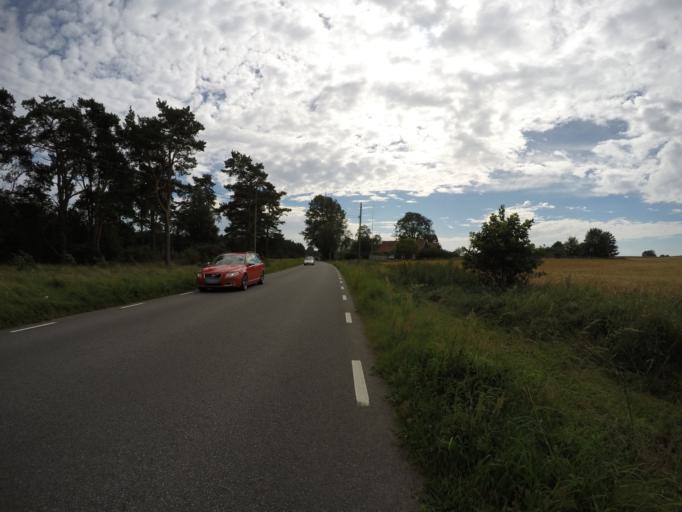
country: SE
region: Skane
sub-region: Simrishamns Kommun
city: Simrishamn
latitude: 55.4329
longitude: 14.2253
